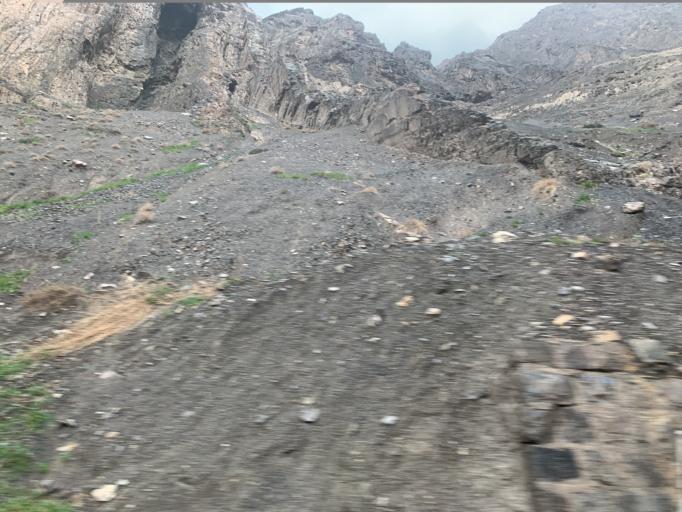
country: IR
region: Mazandaran
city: Amol
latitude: 36.1130
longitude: 52.2814
